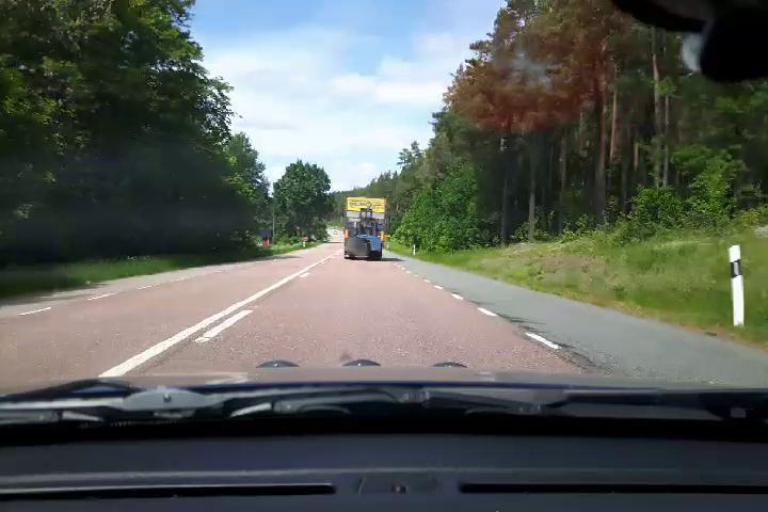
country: SE
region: Uppsala
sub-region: Osthammars Kommun
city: Bjorklinge
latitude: 60.1401
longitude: 17.5047
